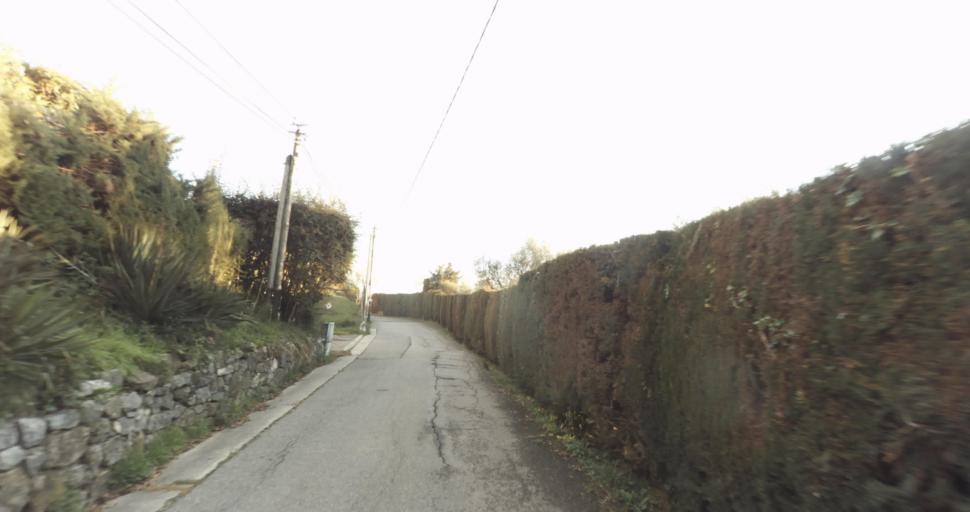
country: FR
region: Provence-Alpes-Cote d'Azur
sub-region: Departement des Alpes-Maritimes
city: Vence
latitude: 43.7296
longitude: 7.0902
